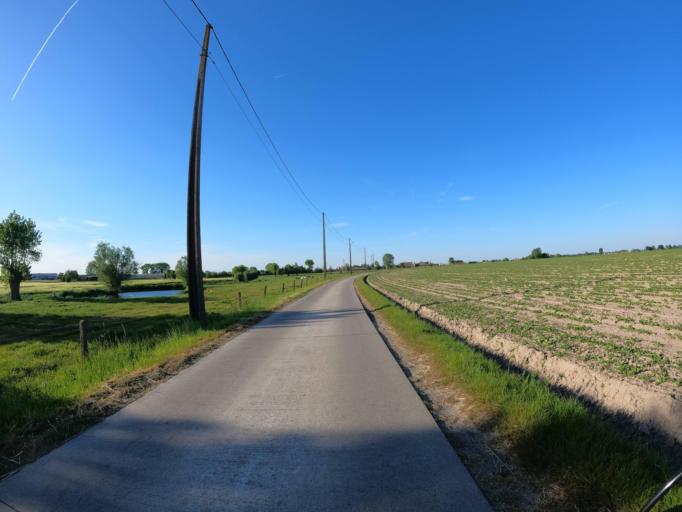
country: BE
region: Flanders
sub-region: Provincie West-Vlaanderen
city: Dentergem
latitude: 50.9981
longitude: 3.4503
